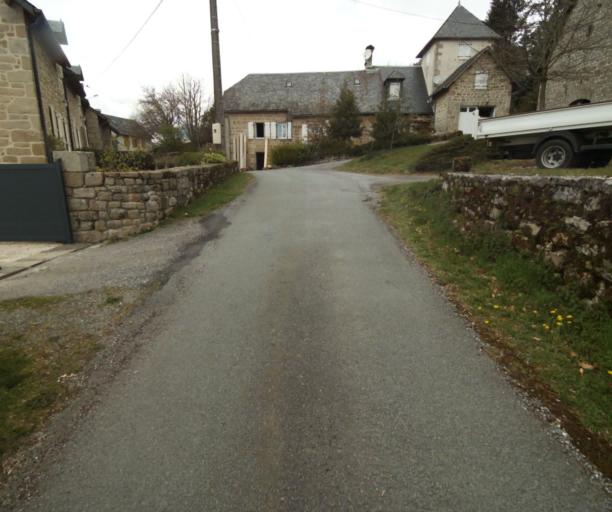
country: FR
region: Limousin
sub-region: Departement de la Correze
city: Correze
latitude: 45.3161
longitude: 1.9283
